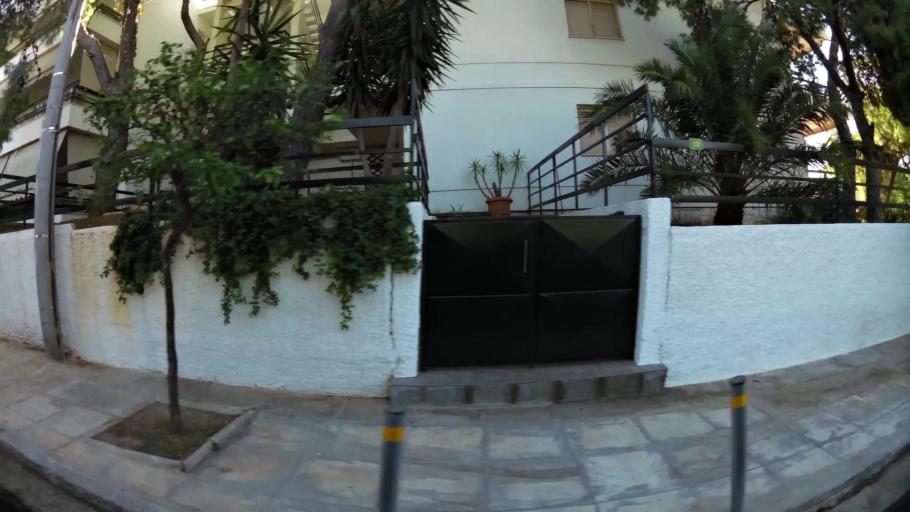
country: GR
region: Attica
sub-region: Nomarchia Anatolikis Attikis
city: Vouliagmeni
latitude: 37.8152
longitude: 23.7849
